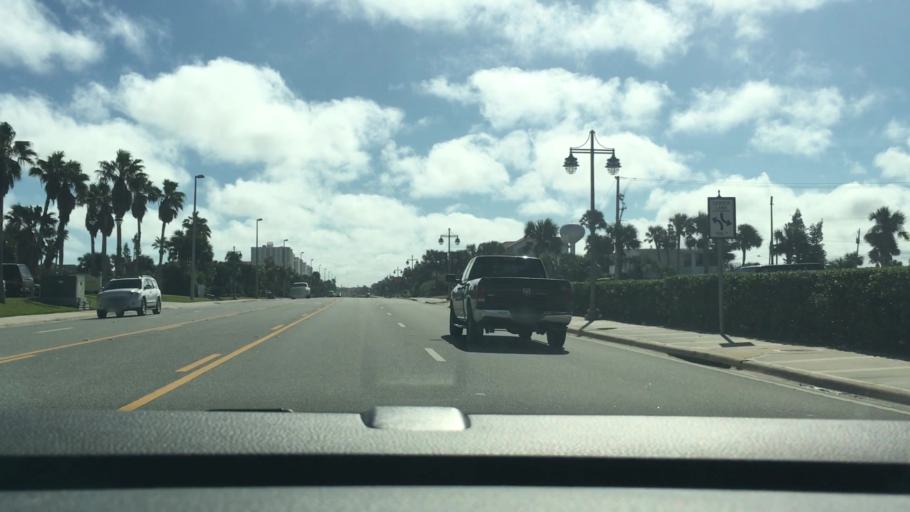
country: US
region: Florida
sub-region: Volusia County
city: Daytona Beach Shores
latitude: 29.1806
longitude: -80.9853
